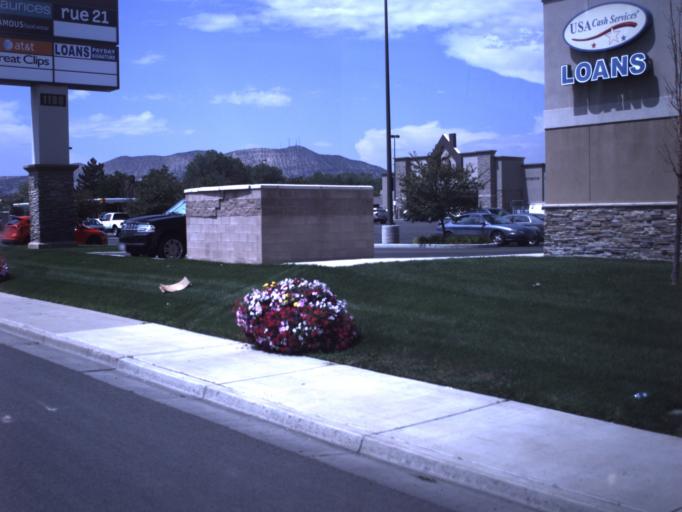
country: US
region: Utah
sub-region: Uintah County
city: Vernal
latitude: 40.4504
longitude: -109.5505
